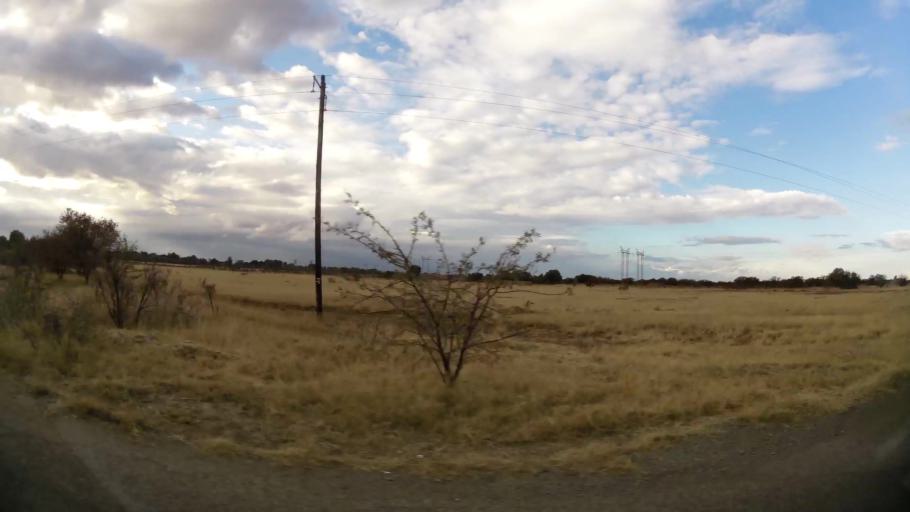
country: ZA
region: Orange Free State
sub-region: Lejweleputswa District Municipality
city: Welkom
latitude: -28.0111
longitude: 26.7126
